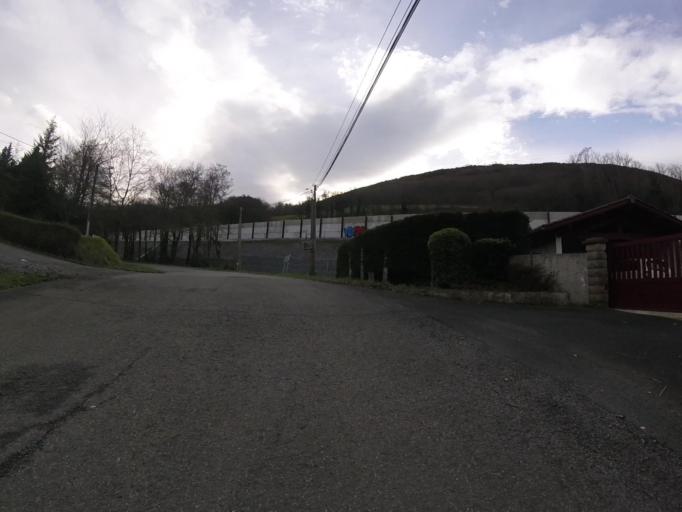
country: FR
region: Aquitaine
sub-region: Departement des Pyrenees-Atlantiques
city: Urrugne
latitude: 43.3416
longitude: -1.7336
